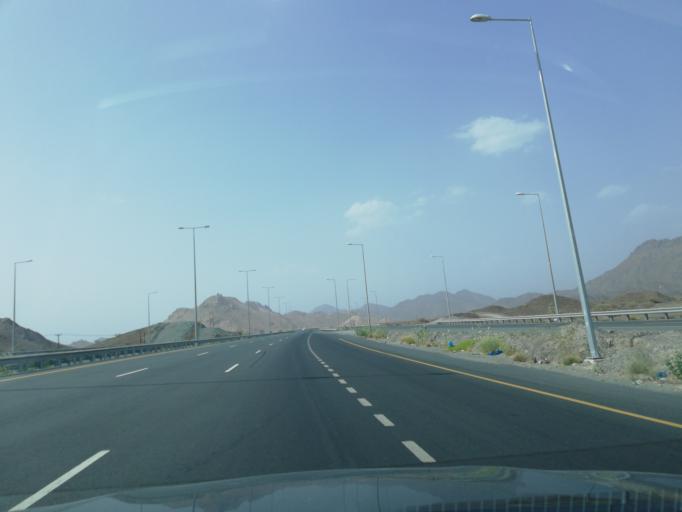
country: OM
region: Ash Sharqiyah
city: Ibra'
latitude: 22.9159
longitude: 58.2638
